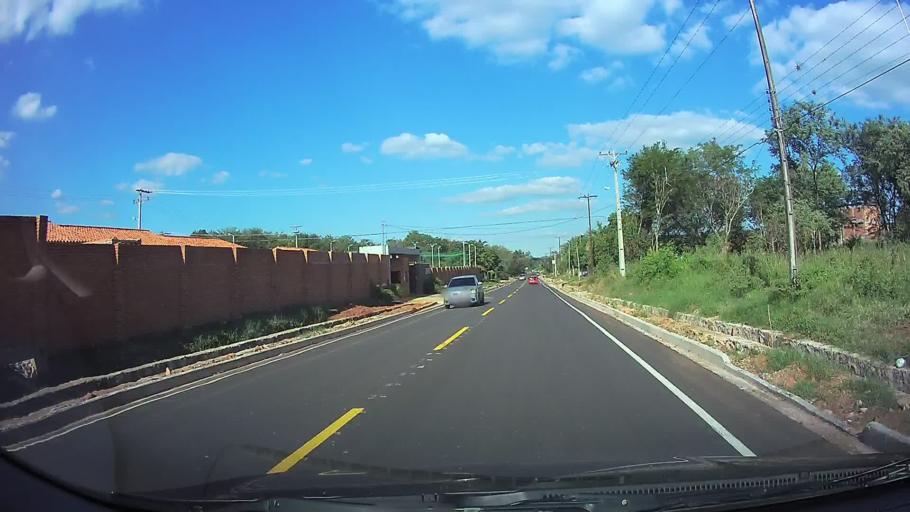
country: PY
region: Central
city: San Lorenzo
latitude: -25.2681
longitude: -57.4682
